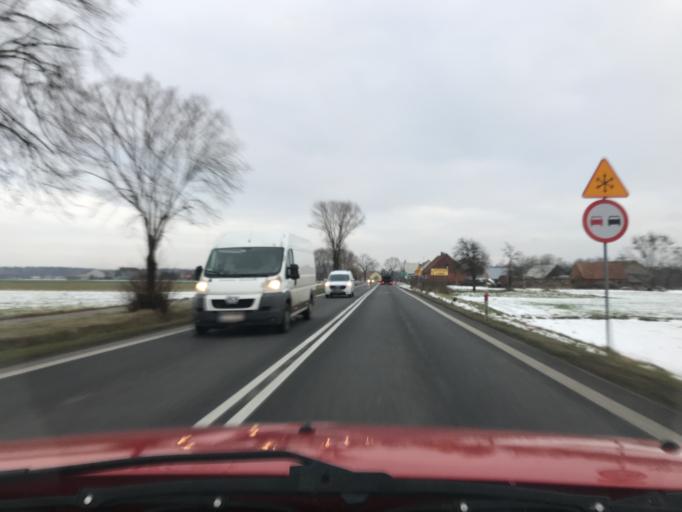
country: PL
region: Greater Poland Voivodeship
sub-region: Powiat pleszewski
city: Pleszew
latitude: 51.8871
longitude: 17.8532
